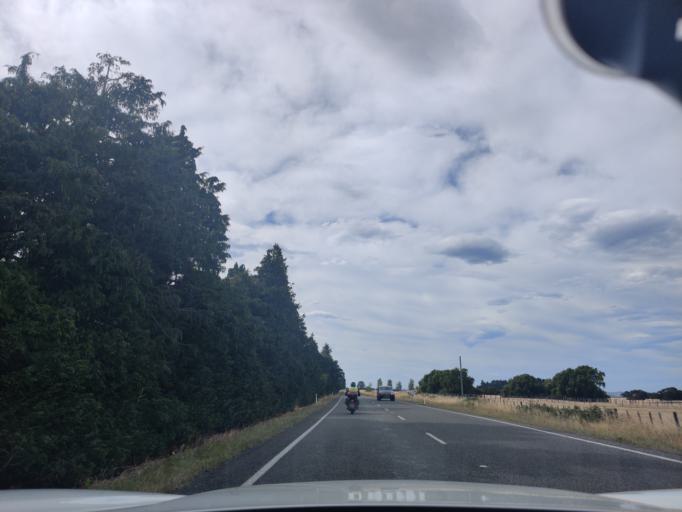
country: NZ
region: Wellington
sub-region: Masterton District
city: Masterton
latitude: -40.8702
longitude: 175.6481
